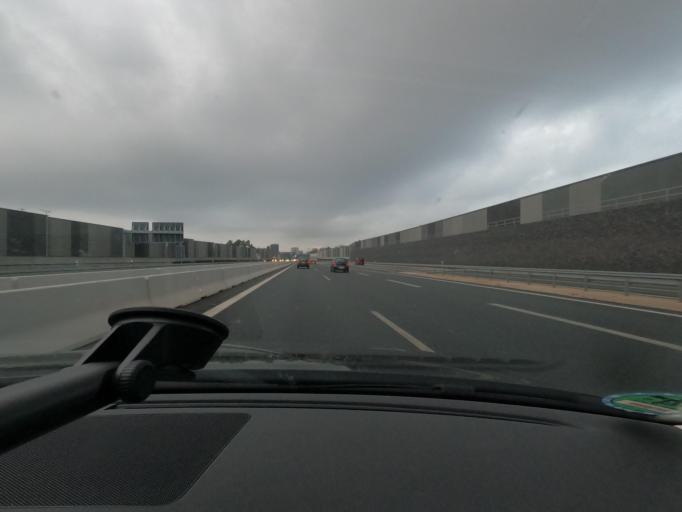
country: DE
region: Bavaria
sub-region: Regierungsbezirk Mittelfranken
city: Erlangen
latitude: 49.5638
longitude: 10.9917
